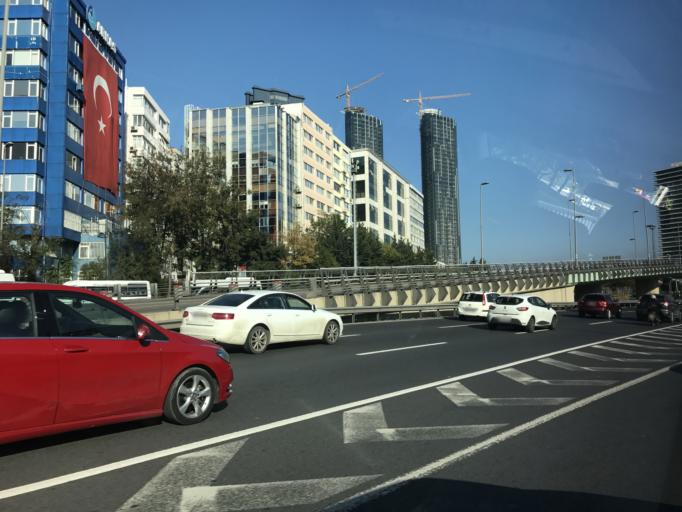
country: TR
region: Istanbul
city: Sisli
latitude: 41.0674
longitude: 29.0094
